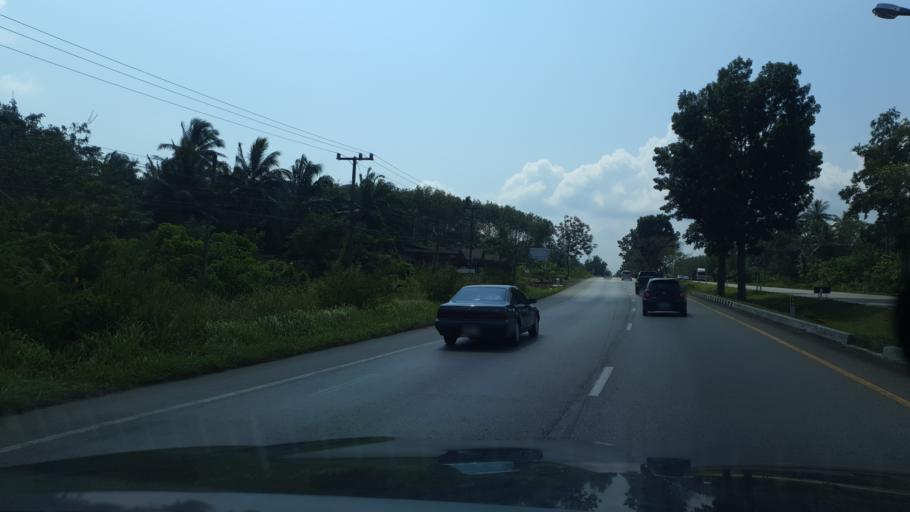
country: TH
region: Chumphon
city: Chumphon
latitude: 10.3744
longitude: 99.1272
